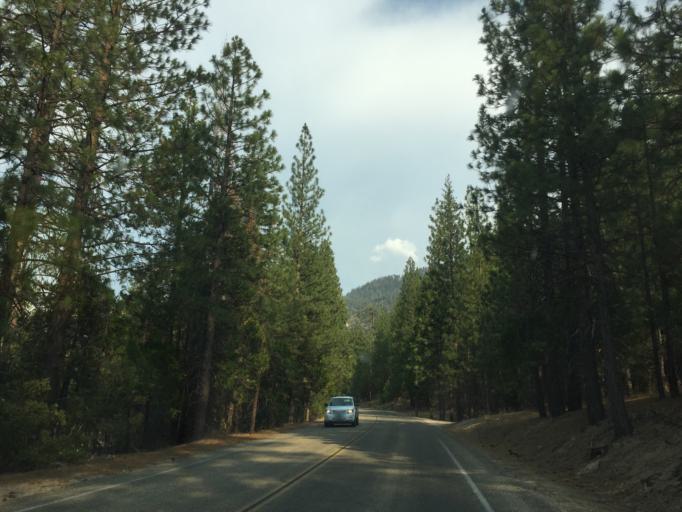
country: US
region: California
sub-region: Tulare County
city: Three Rivers
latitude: 36.7880
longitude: -118.6688
